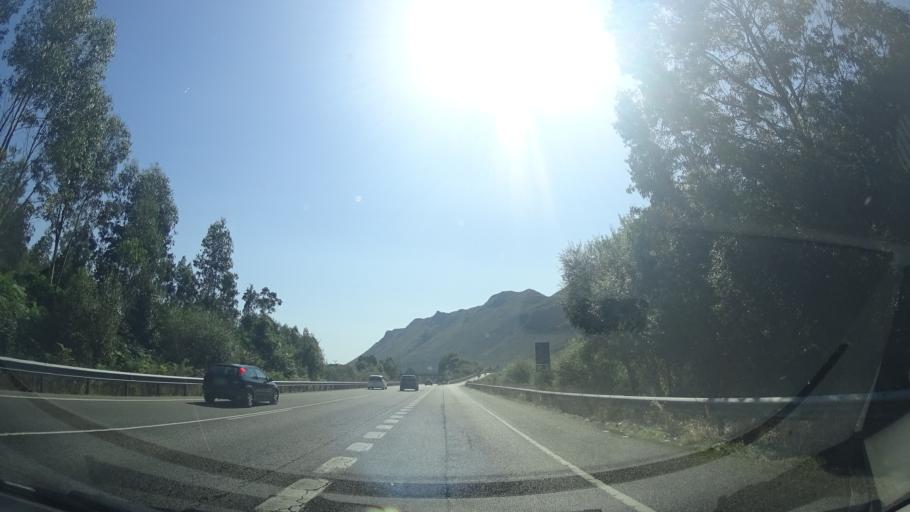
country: ES
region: Asturias
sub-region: Province of Asturias
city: Ribadesella
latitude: 43.4376
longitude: -5.0187
